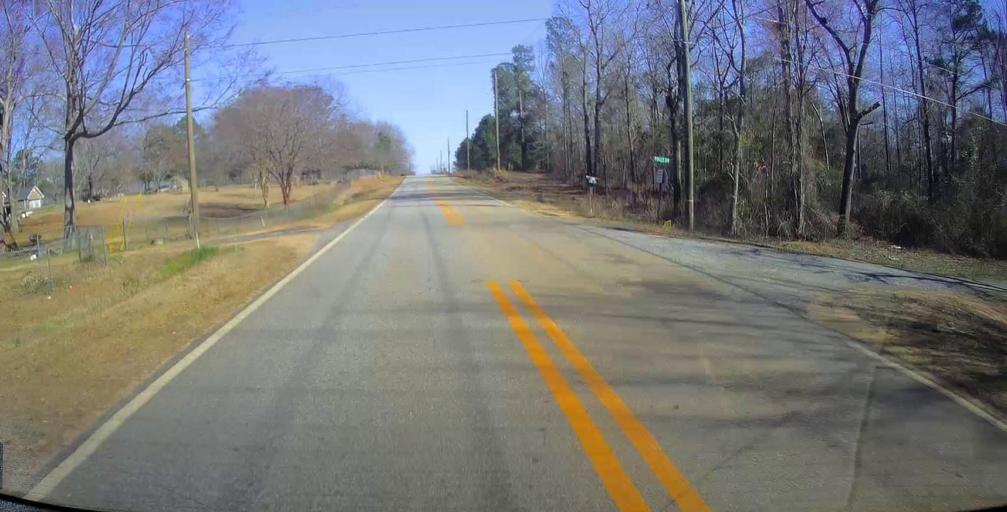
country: US
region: Georgia
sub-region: Peach County
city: Byron
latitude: 32.6193
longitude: -83.7771
